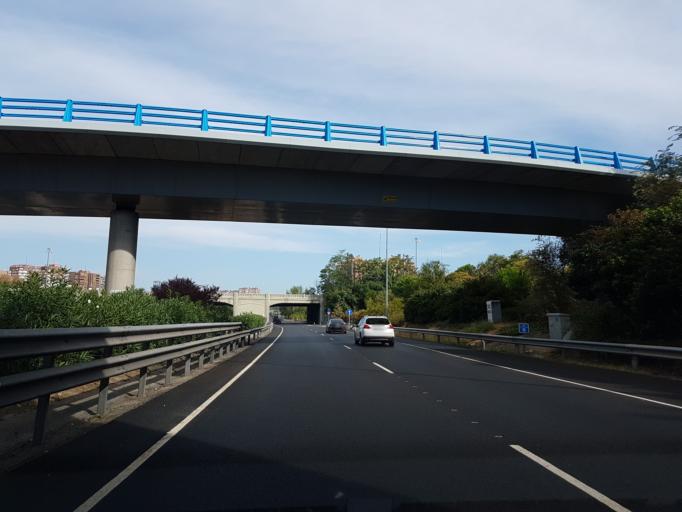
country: ES
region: Madrid
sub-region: Provincia de Madrid
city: Ciudad Lineal
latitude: 40.4433
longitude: -3.6594
